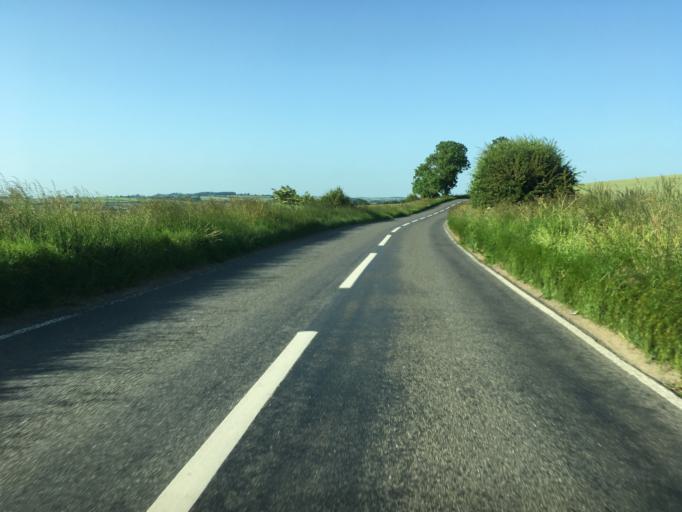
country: GB
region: England
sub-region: Oxfordshire
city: Shipton under Wychwood
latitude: 51.8506
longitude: -1.5798
